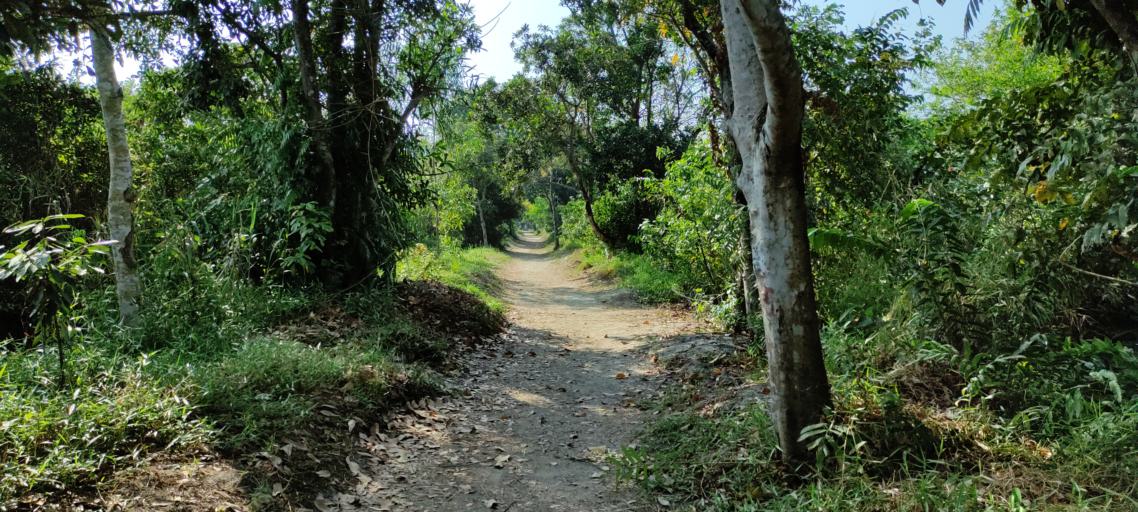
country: IN
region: Kerala
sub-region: Alappuzha
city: Shertallai
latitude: 9.6189
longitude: 76.3850
